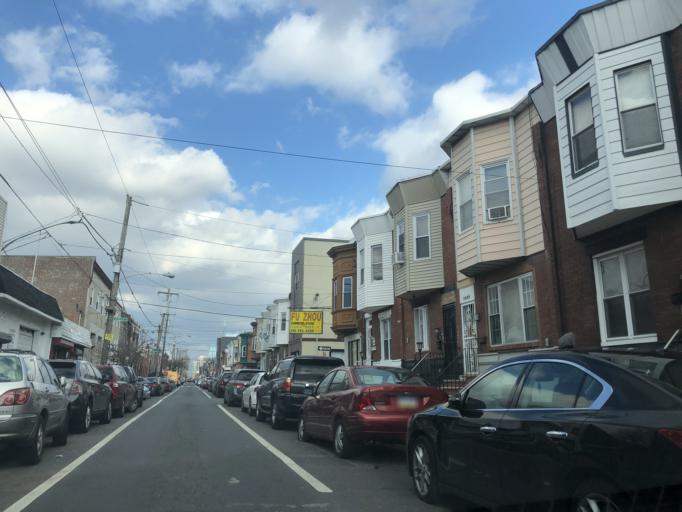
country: US
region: Pennsylvania
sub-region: Philadelphia County
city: Philadelphia
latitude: 39.9269
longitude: -75.1790
